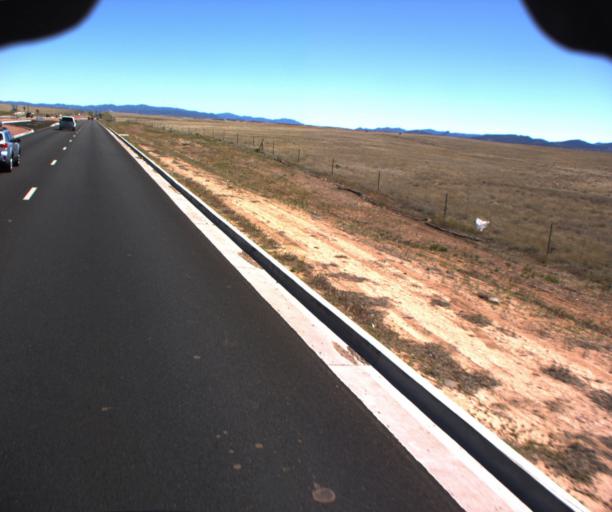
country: US
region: Arizona
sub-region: Yavapai County
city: Chino Valley
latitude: 34.7116
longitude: -112.4525
